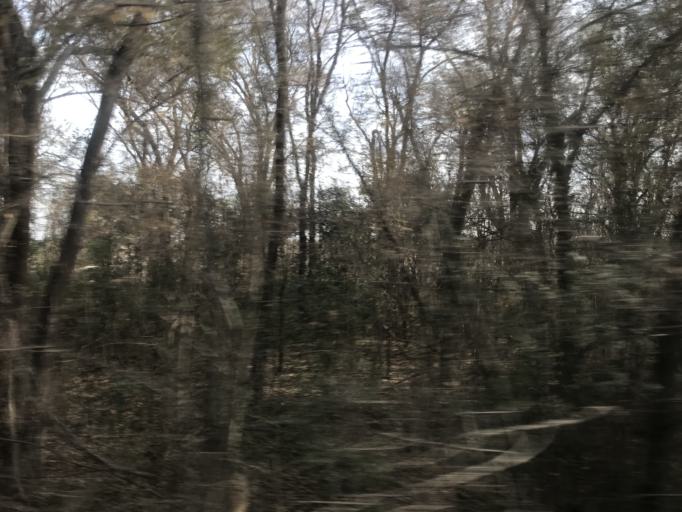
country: AR
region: Cordoba
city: Laguna Larga
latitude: -31.7382
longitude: -63.8367
